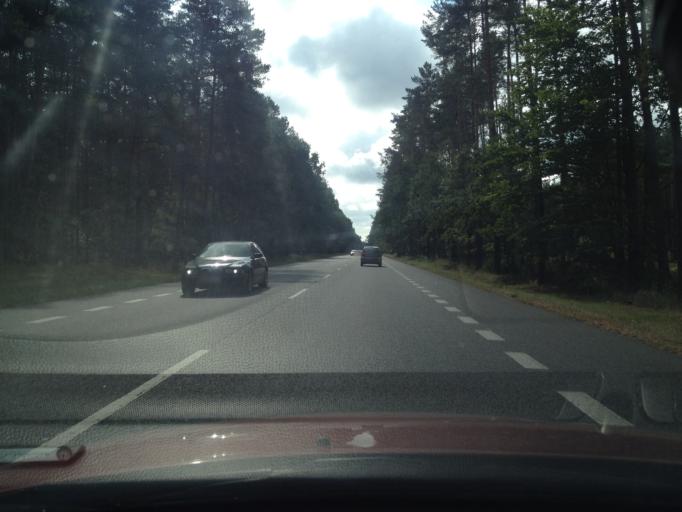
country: PL
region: West Pomeranian Voivodeship
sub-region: Powiat goleniowski
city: Przybiernow
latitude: 53.7040
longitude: 14.7828
